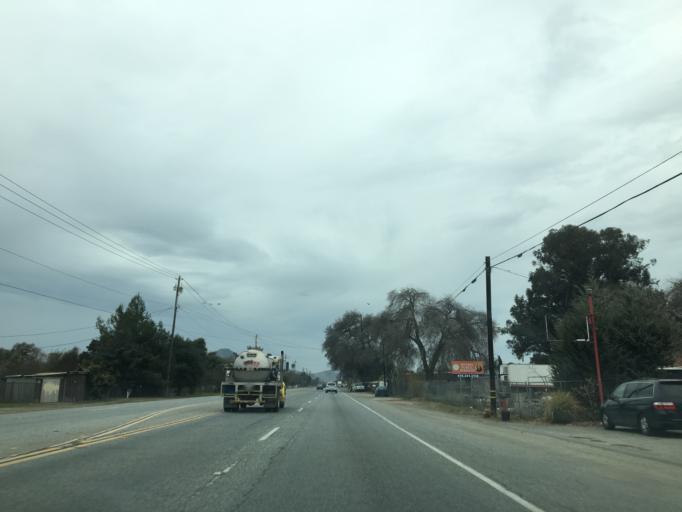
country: US
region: California
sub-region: Santa Clara County
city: San Martin
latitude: 37.0986
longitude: -121.6206
